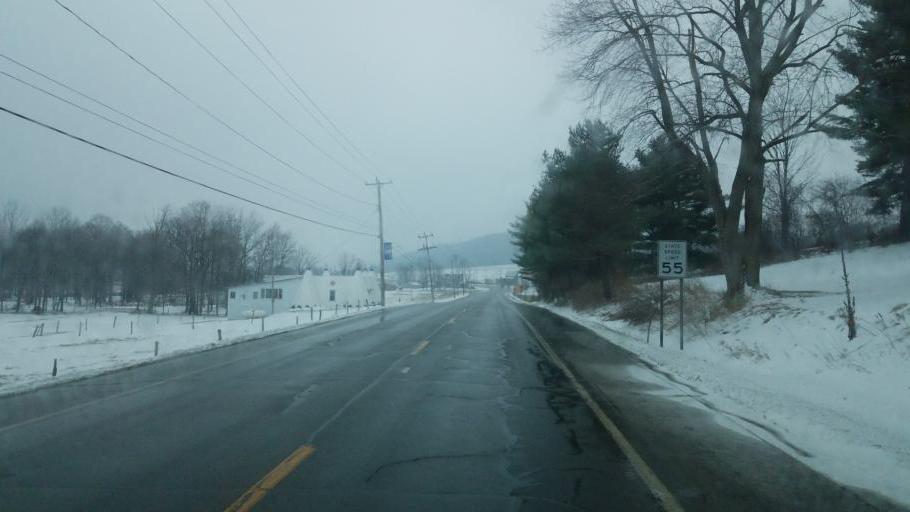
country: US
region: New York
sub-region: Steuben County
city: Canisteo
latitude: 42.1164
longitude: -77.4952
